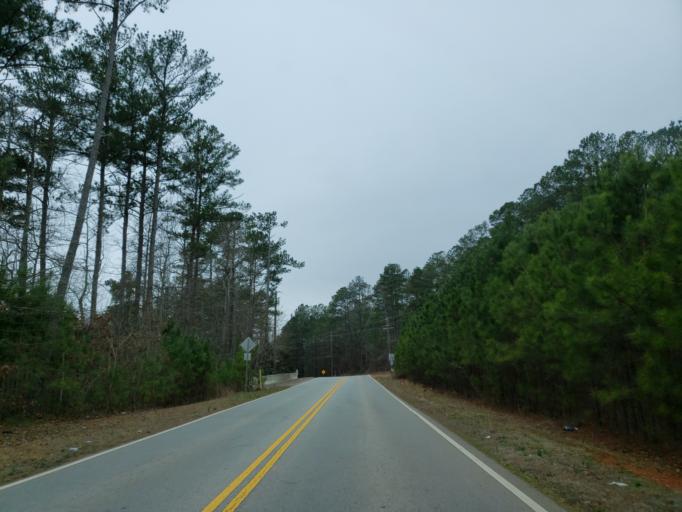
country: US
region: Georgia
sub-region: Paulding County
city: Hiram
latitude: 33.9371
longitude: -84.7127
